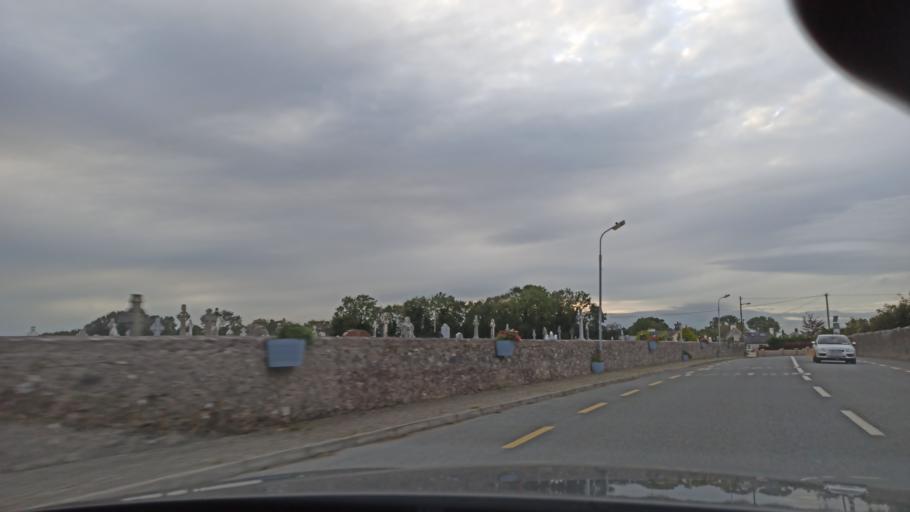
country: IE
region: Munster
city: Cashel
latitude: 52.4710
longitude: -7.8347
